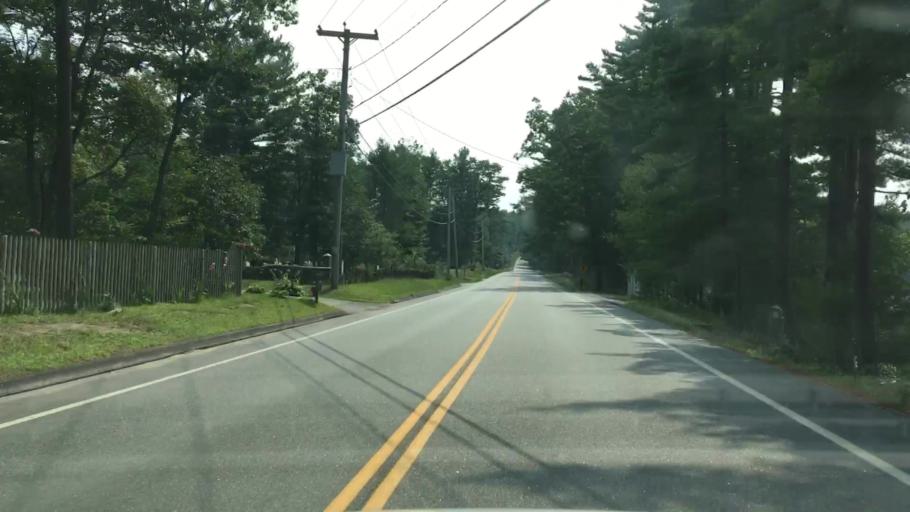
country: US
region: Maine
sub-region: Androscoggin County
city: Livermore
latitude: 44.3356
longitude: -70.2704
